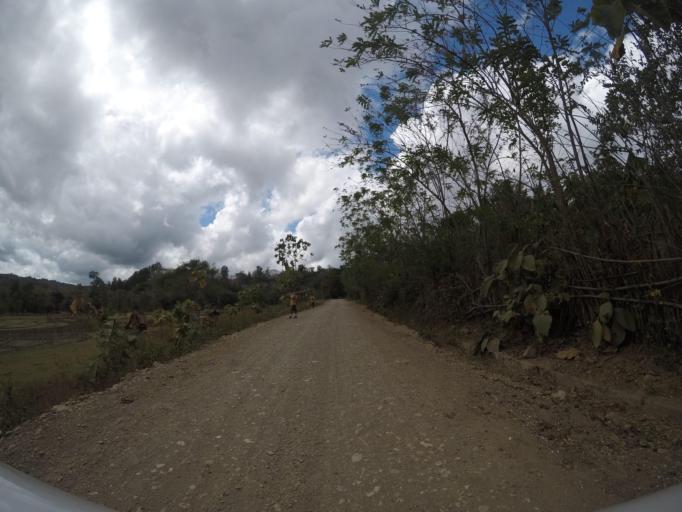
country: TL
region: Lautem
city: Lospalos
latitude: -8.5204
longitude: 126.8394
